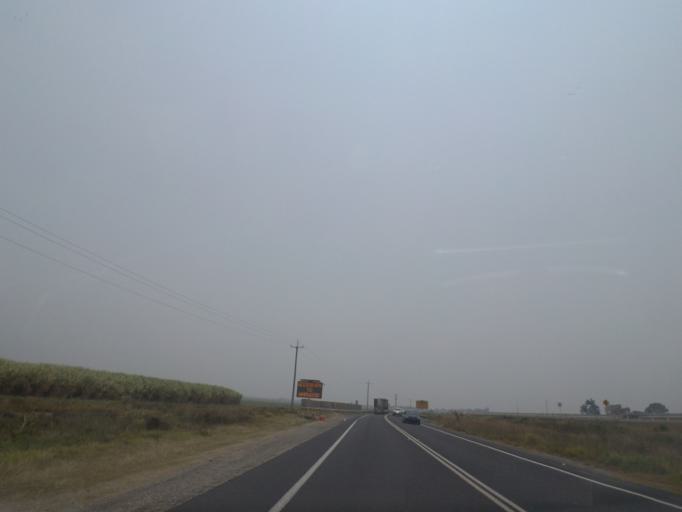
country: AU
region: New South Wales
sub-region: Clarence Valley
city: Maclean
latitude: -29.4155
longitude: 153.2411
